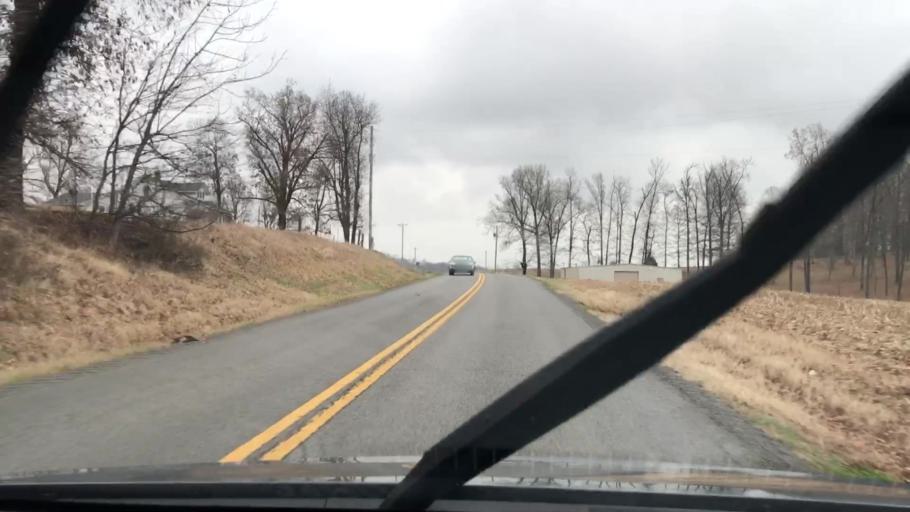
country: US
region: Kentucky
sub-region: Webster County
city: Sebree
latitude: 37.4902
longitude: -87.4632
